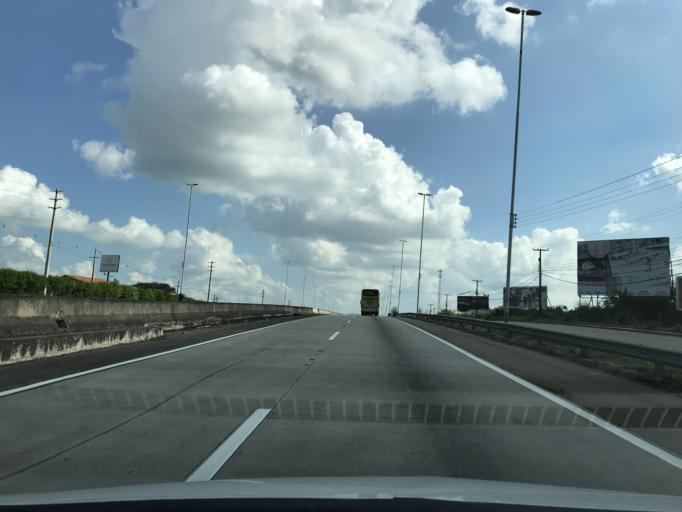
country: BR
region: Pernambuco
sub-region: Gravata
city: Gravata
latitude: -8.1990
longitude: -35.5869
